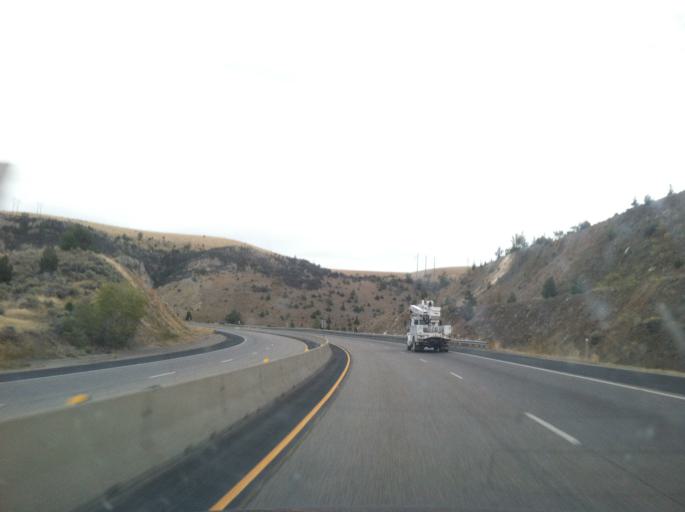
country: US
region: Montana
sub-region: Jefferson County
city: Whitehall
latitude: 45.8767
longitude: -111.8963
